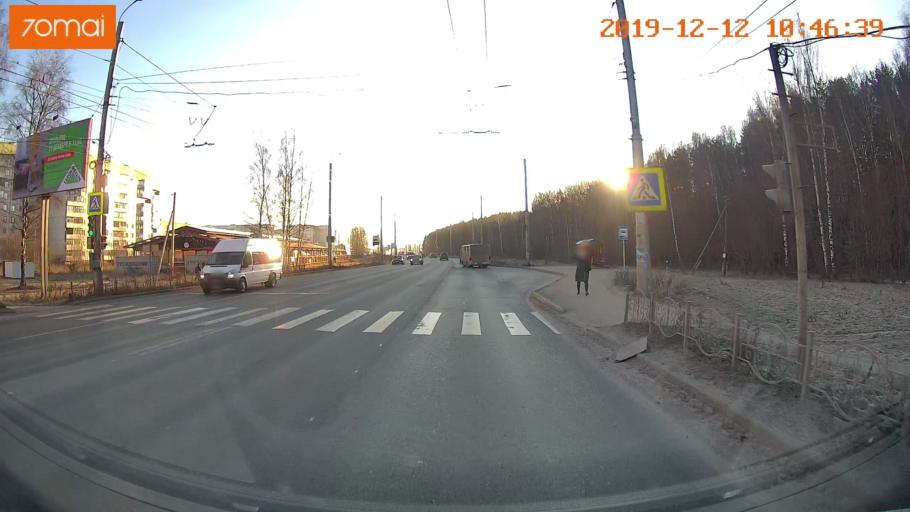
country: RU
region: Ivanovo
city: Kokhma
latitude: 56.9518
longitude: 41.0457
